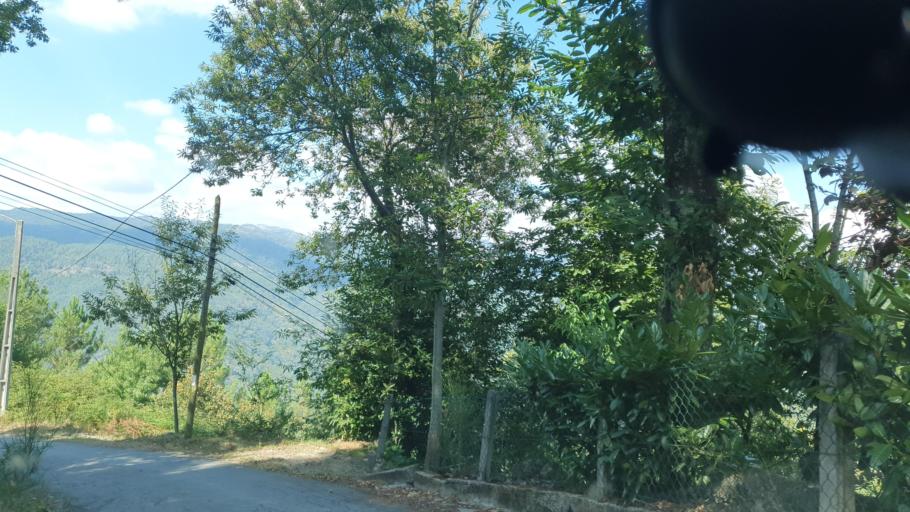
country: PT
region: Braga
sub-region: Vieira do Minho
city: Vieira do Minho
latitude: 41.6751
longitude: -8.1353
